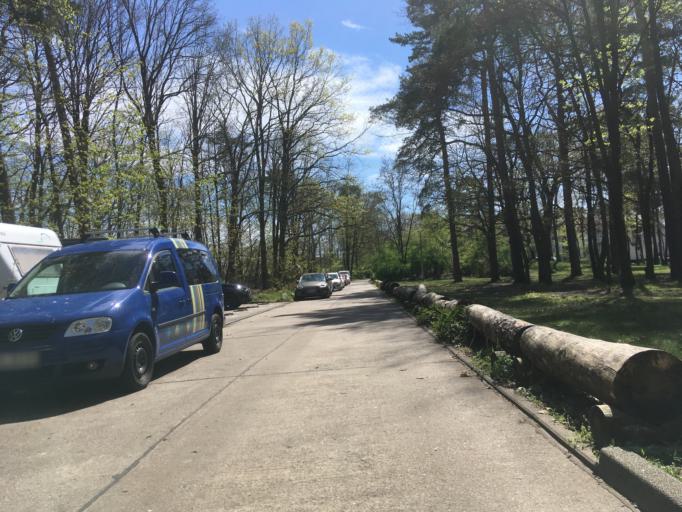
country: DE
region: Brandenburg
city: Erkner
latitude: 52.4352
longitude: 13.7565
